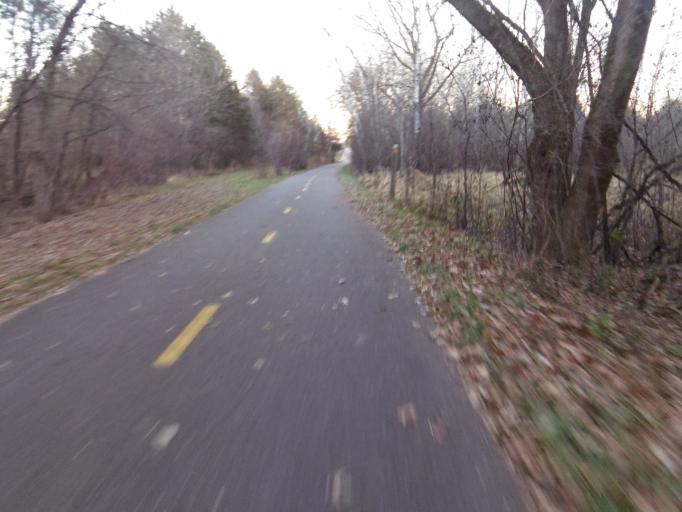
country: US
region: Minnesota
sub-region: Washington County
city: Grant
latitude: 45.1022
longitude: -92.8680
